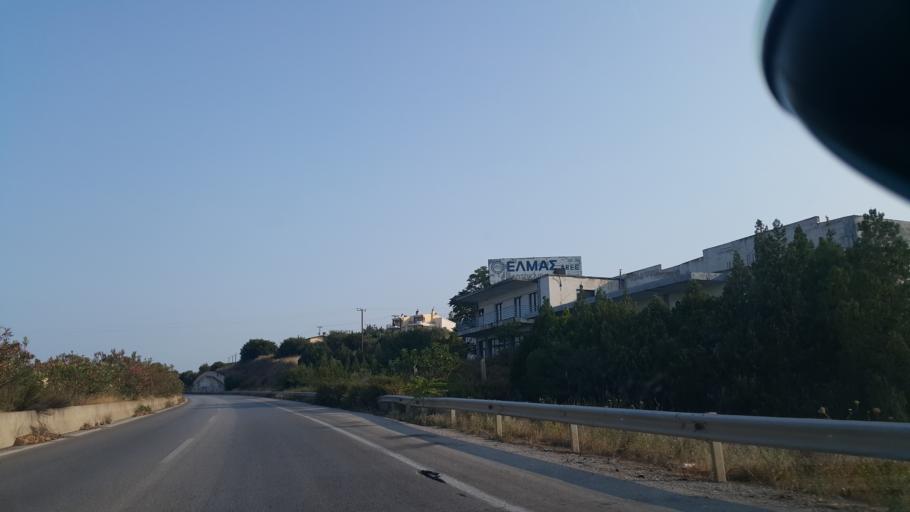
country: GR
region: Central Macedonia
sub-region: Nomos Thessalonikis
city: Kardia
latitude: 40.4498
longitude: 23.0100
